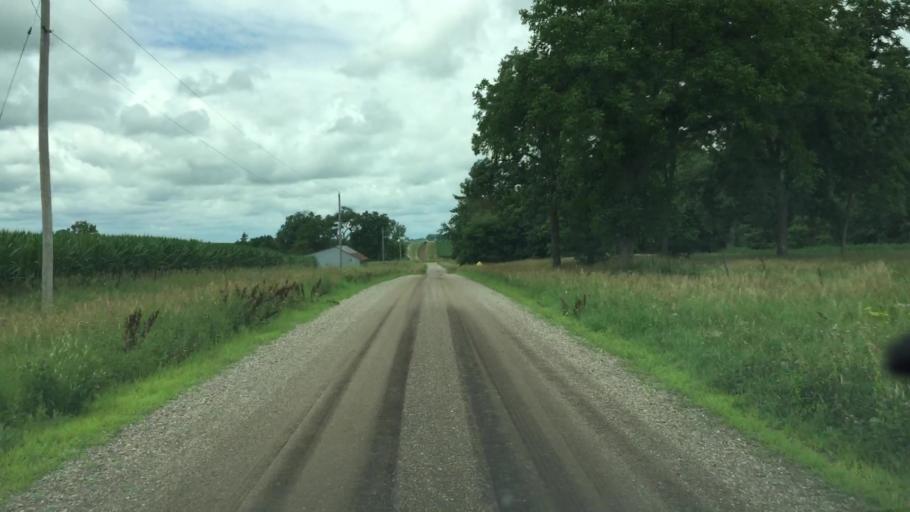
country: US
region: Iowa
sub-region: Jasper County
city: Monroe
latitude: 41.5662
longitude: -93.1156
